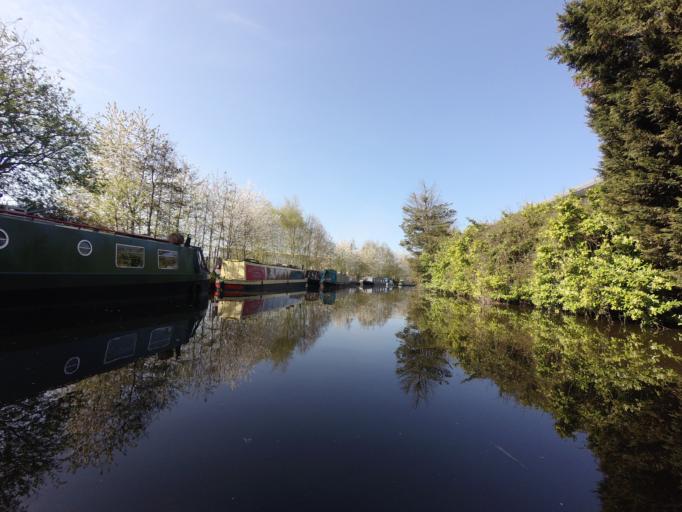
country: GB
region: England
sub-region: Greater London
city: Greenford
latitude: 51.5470
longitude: -0.3461
